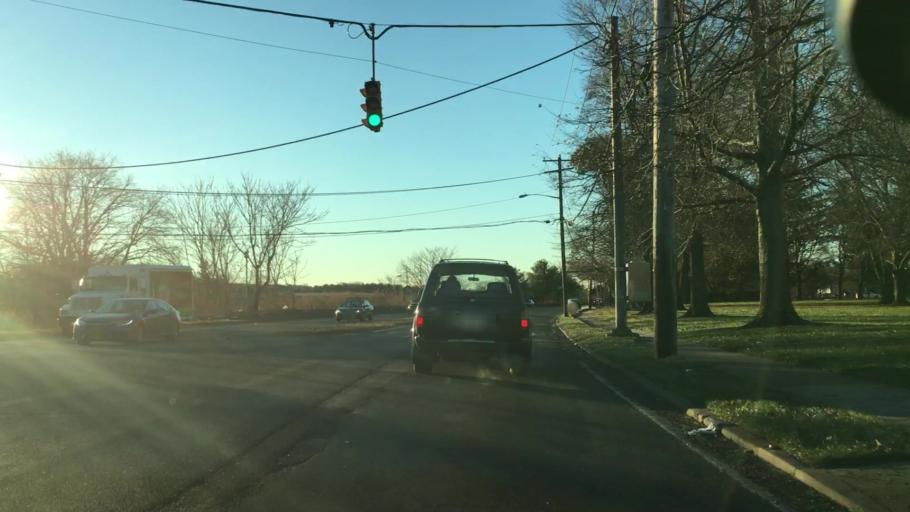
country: US
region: New York
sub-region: Suffolk County
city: Melville
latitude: 40.7781
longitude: -73.4052
